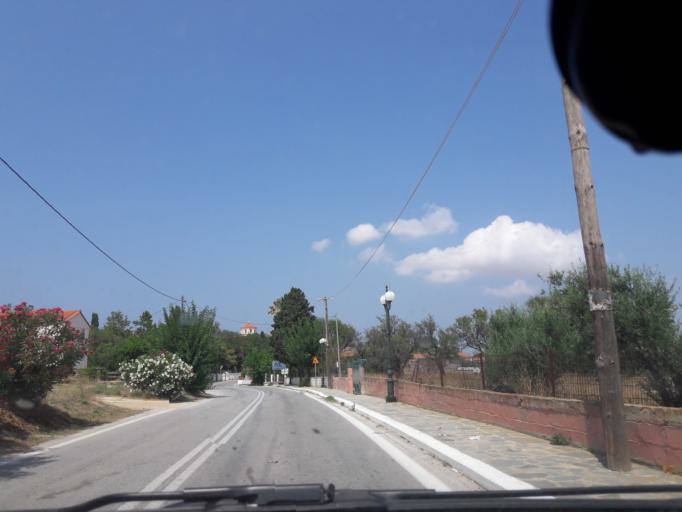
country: GR
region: North Aegean
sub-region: Nomos Lesvou
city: Myrina
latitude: 39.9243
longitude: 25.3311
